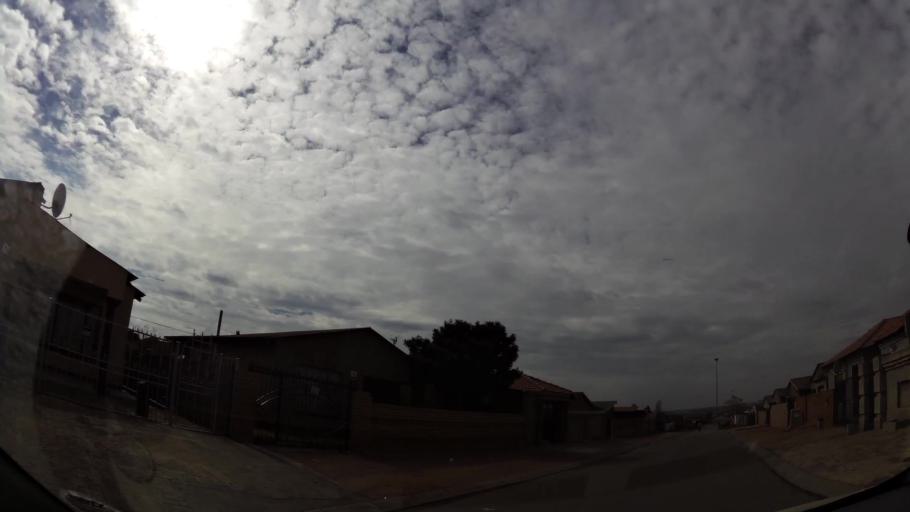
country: ZA
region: Gauteng
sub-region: Ekurhuleni Metropolitan Municipality
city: Germiston
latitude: -26.3722
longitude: 28.1643
